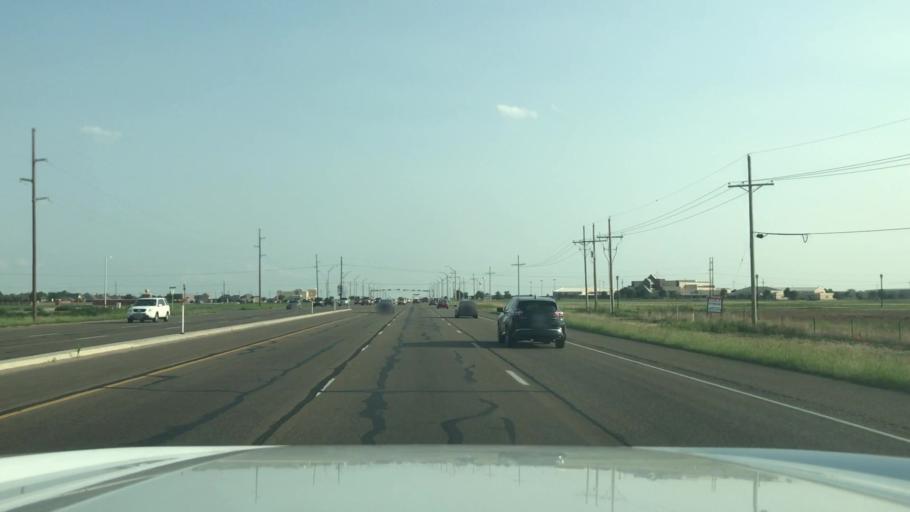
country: US
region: Texas
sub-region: Potter County
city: Amarillo
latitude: 35.1512
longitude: -101.9383
